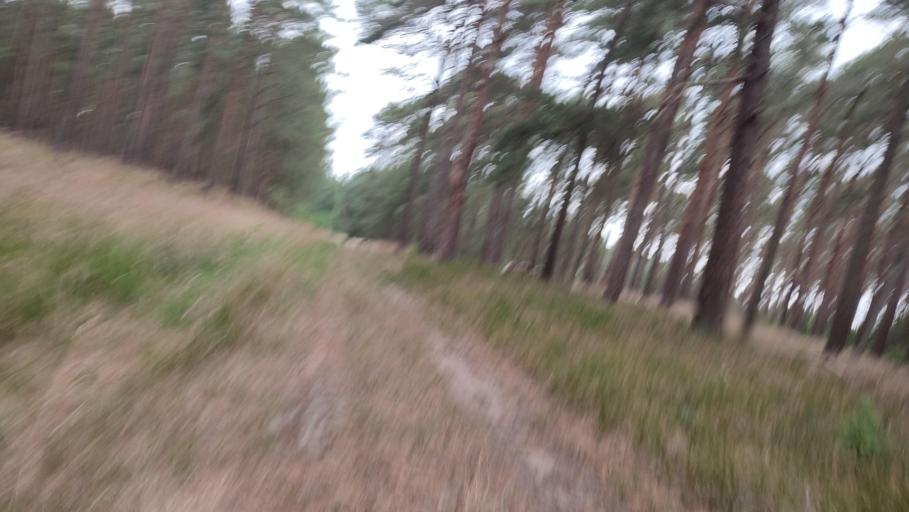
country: DE
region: Lower Saxony
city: Hitzacker
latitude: 53.1999
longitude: 11.0897
